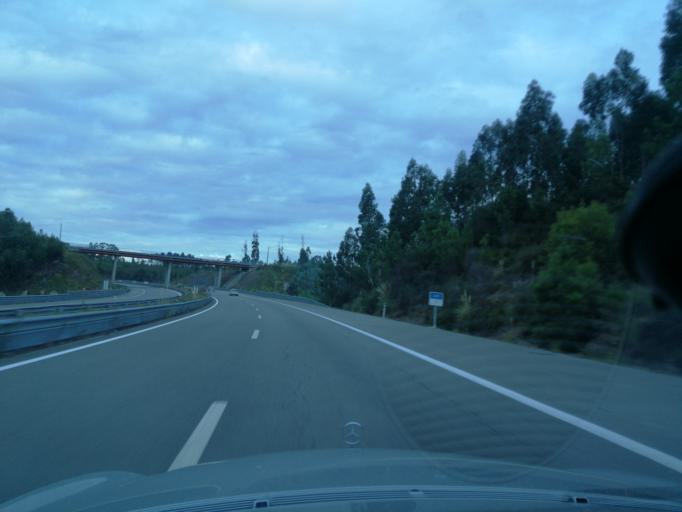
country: PT
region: Aveiro
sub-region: Estarreja
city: Salreu
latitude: 40.6935
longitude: -8.5352
